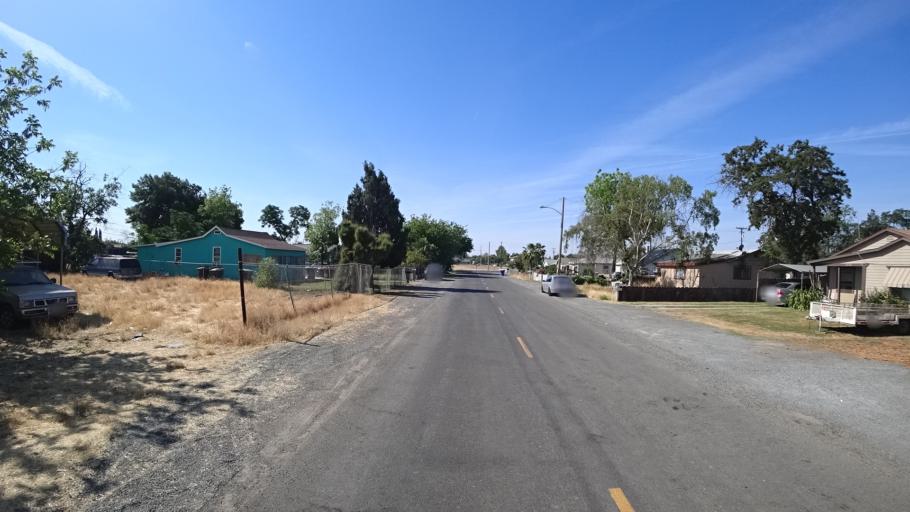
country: US
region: California
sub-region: Kings County
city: Hanford
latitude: 36.3455
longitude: -119.6356
